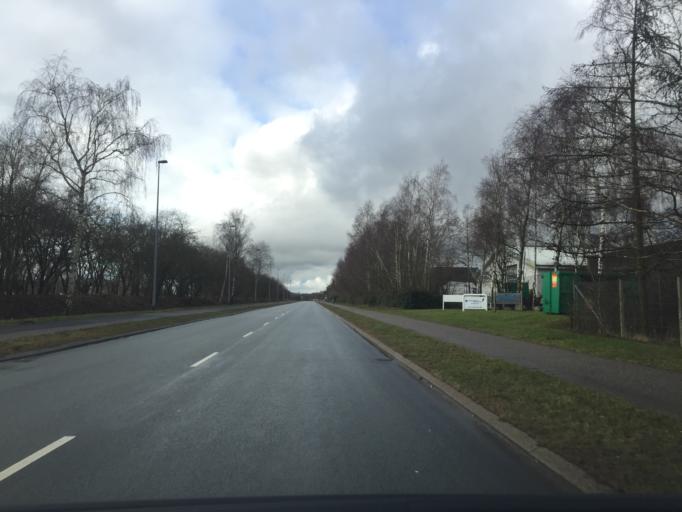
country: DK
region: Capital Region
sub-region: Fureso Kommune
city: Farum
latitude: 55.8187
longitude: 12.3591
